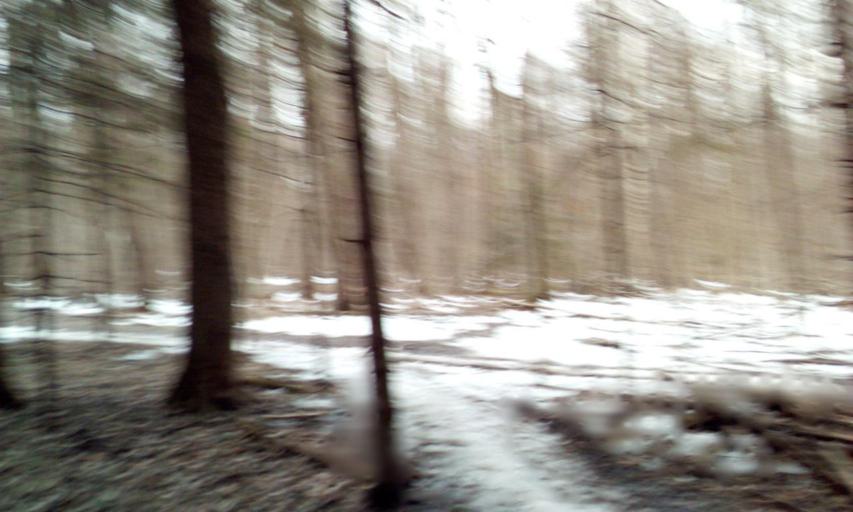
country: RU
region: Moskovskaya
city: Annino
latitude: 55.5536
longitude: 37.2729
